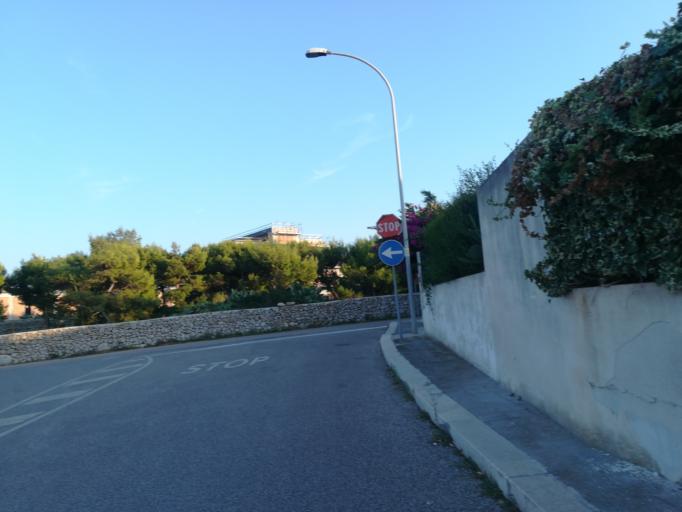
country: IT
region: Apulia
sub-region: Provincia di Bari
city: Polignano a Mare
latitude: 40.9905
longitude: 17.2322
